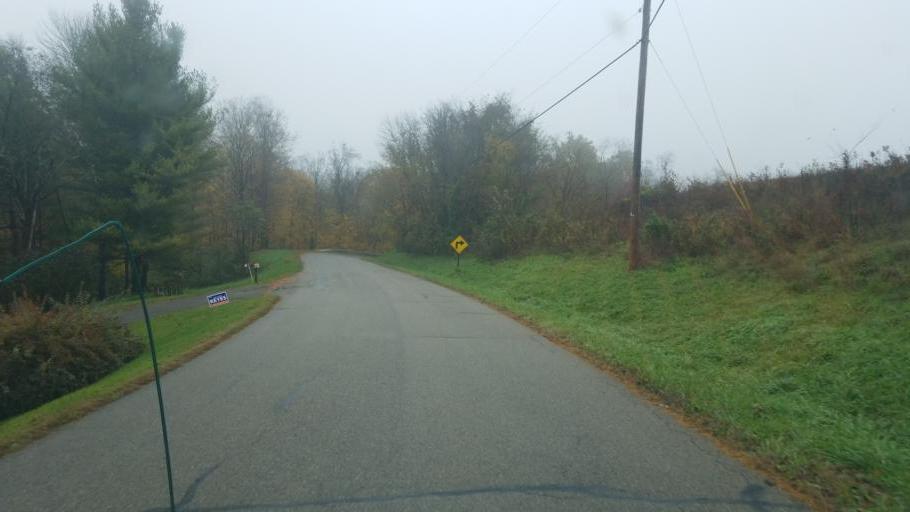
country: US
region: Ohio
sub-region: Morgan County
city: McConnelsville
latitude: 39.6345
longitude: -81.8756
